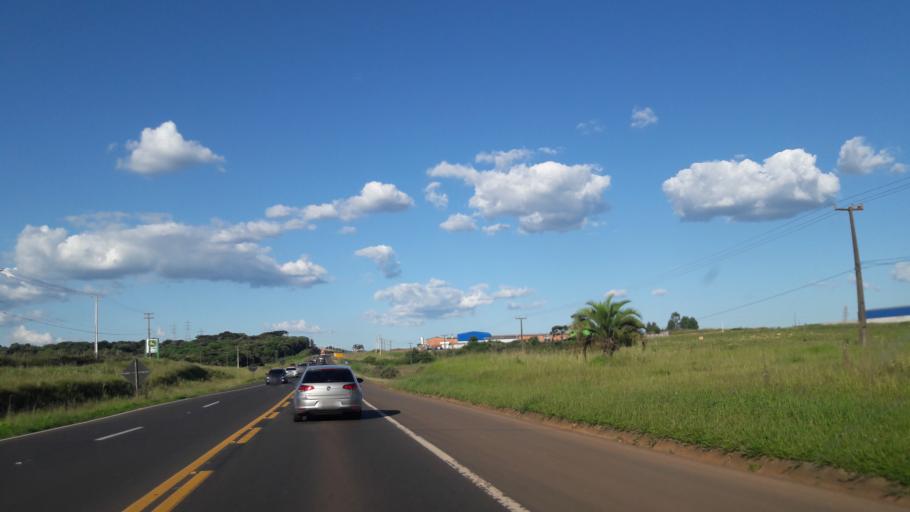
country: BR
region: Parana
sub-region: Guarapuava
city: Guarapuava
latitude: -25.3760
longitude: -51.5031
